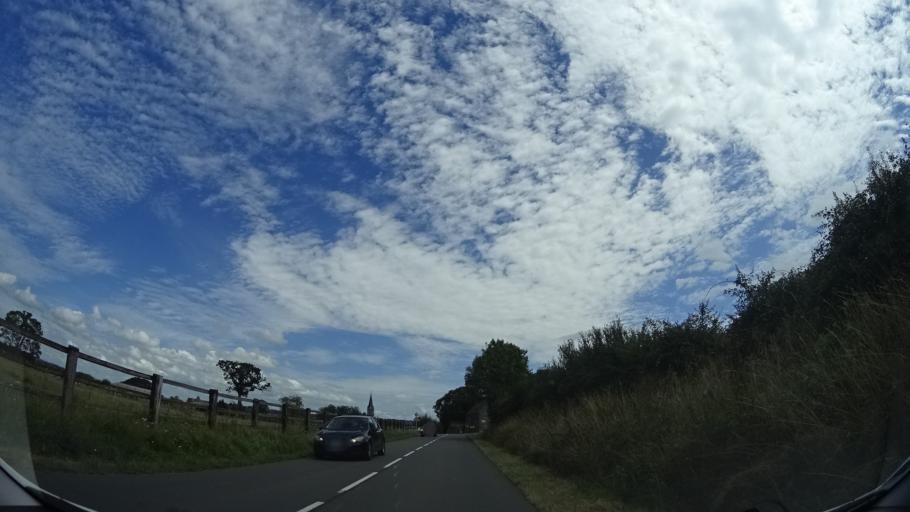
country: FR
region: Lower Normandy
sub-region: Departement de la Manche
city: Marcey-les-Greves
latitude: 48.6827
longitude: -1.4161
